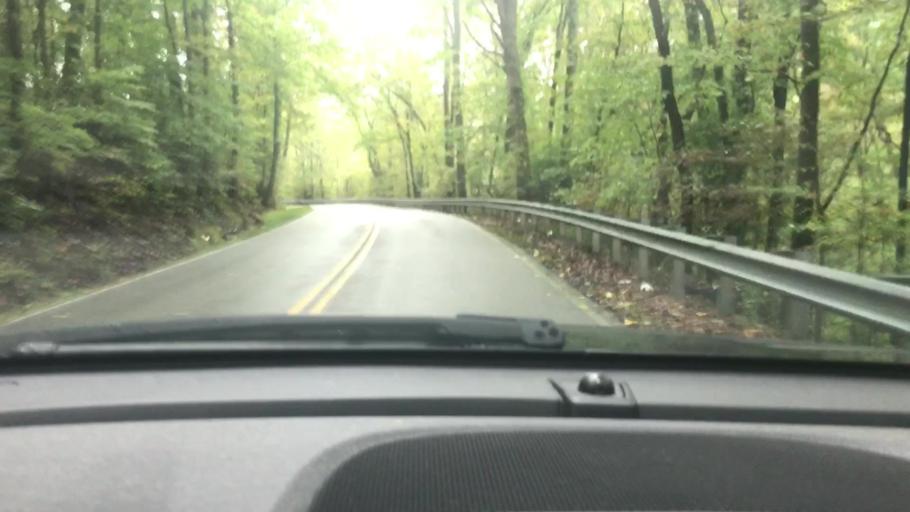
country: US
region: Tennessee
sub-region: Cheatham County
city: Kingston Springs
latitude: 36.1015
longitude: -87.1352
